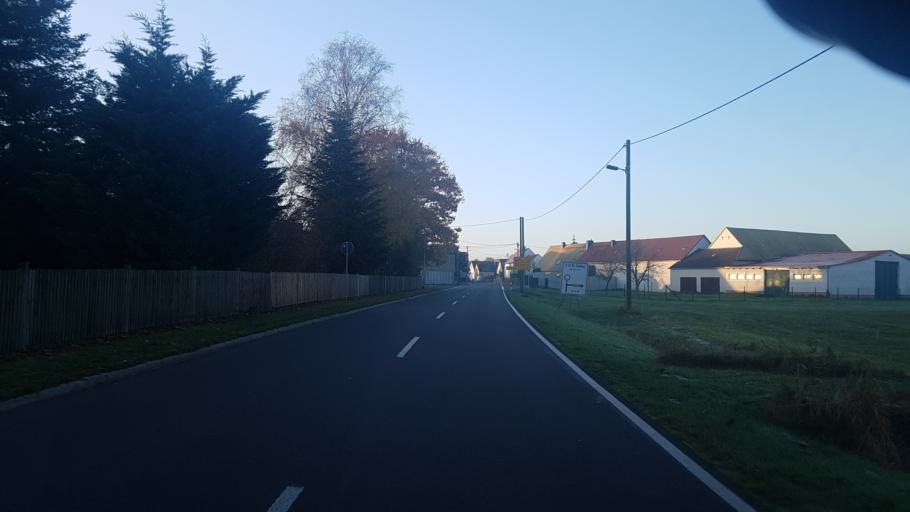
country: DE
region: Saxony
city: Schildau
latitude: 51.4523
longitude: 12.9719
